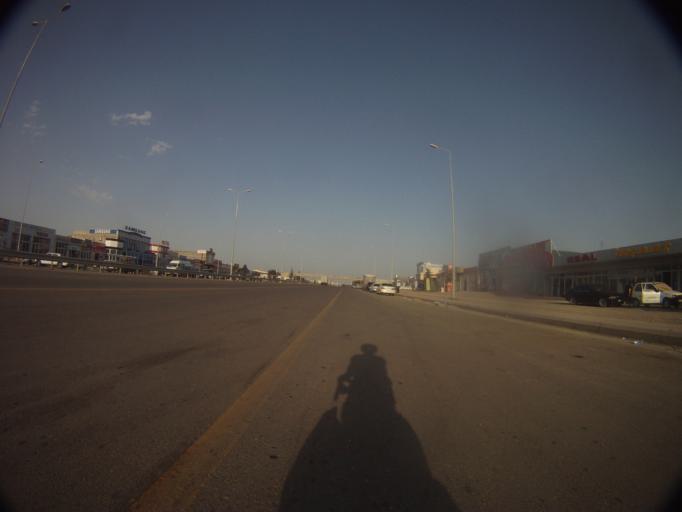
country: AZ
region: Goranboy
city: Goranboy
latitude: 40.6491
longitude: 46.8192
